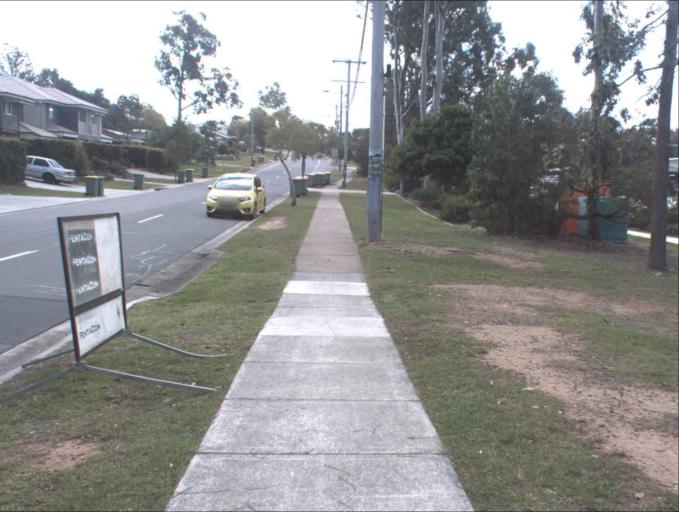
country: AU
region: Queensland
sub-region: Logan
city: Park Ridge South
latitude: -27.6691
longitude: 153.0231
